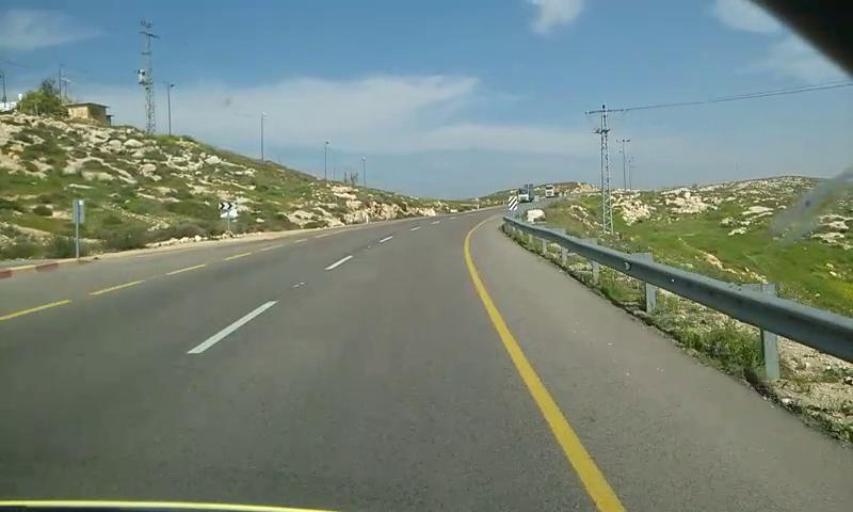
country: PS
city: Rabud
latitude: 31.3927
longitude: 35.0167
